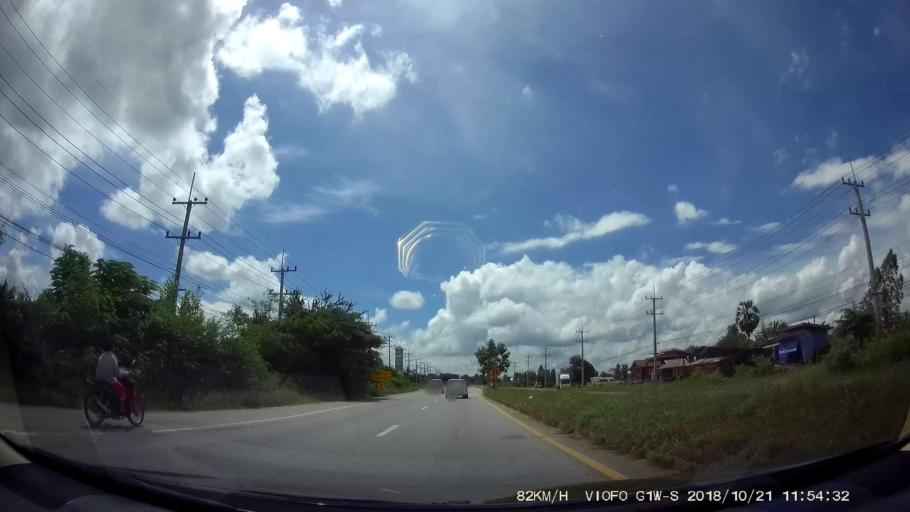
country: TH
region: Chaiyaphum
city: Chatturat
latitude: 15.5835
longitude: 101.9004
